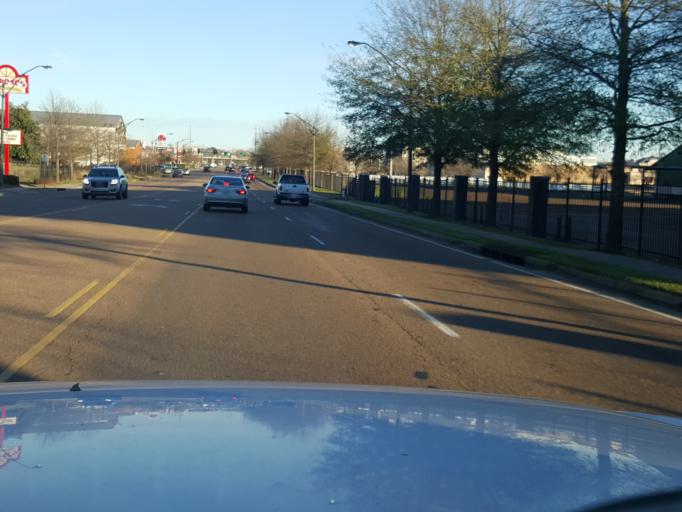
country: US
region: Mississippi
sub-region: Hinds County
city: Jackson
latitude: 32.3039
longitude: -90.1750
